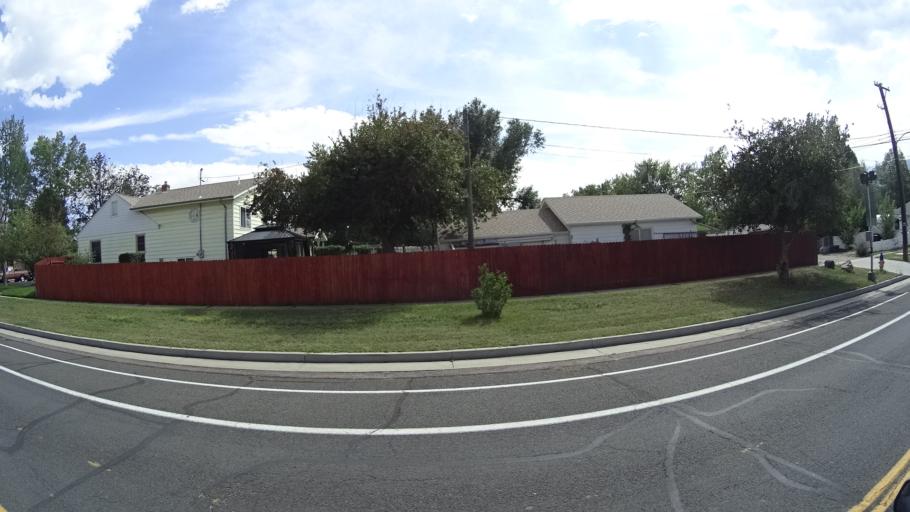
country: US
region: Colorado
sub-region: El Paso County
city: Colorado Springs
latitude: 38.8458
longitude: -104.7990
